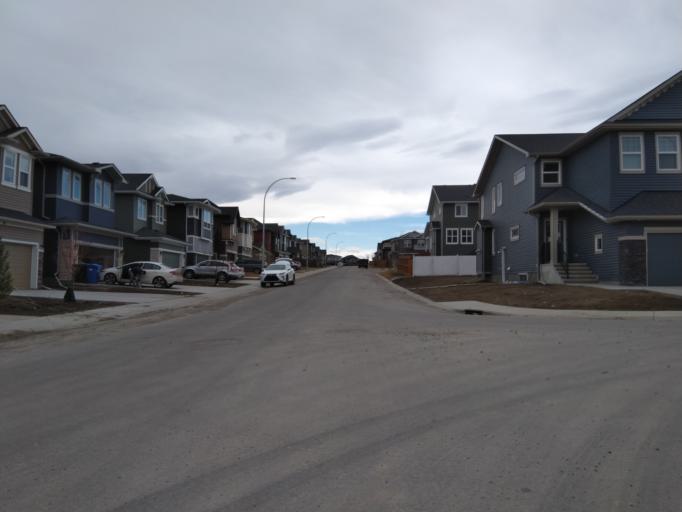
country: CA
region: Alberta
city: Calgary
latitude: 51.1775
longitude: -114.0958
